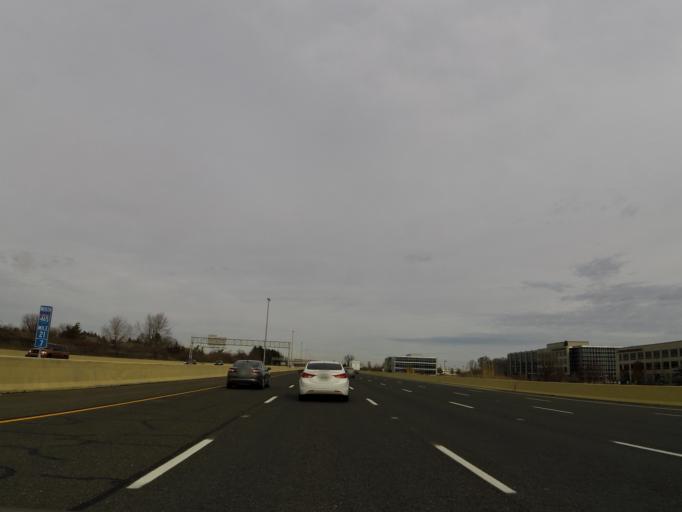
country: US
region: Indiana
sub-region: Boone County
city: Zionsville
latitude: 39.8892
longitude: -86.2694
